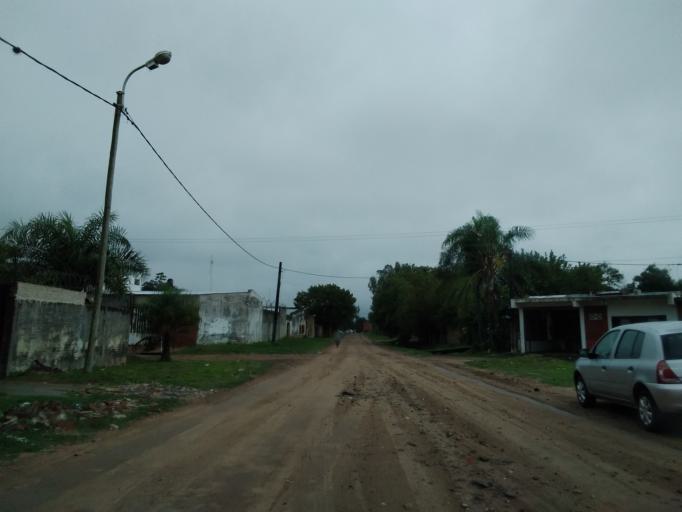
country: AR
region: Corrientes
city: Corrientes
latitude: -27.4857
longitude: -58.8225
